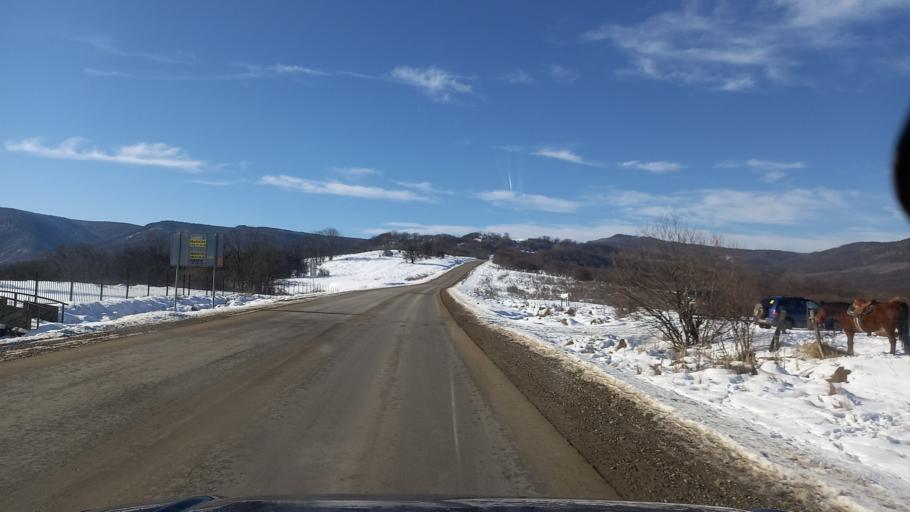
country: RU
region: Adygeya
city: Kamennomostskiy
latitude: 44.2336
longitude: 40.1472
